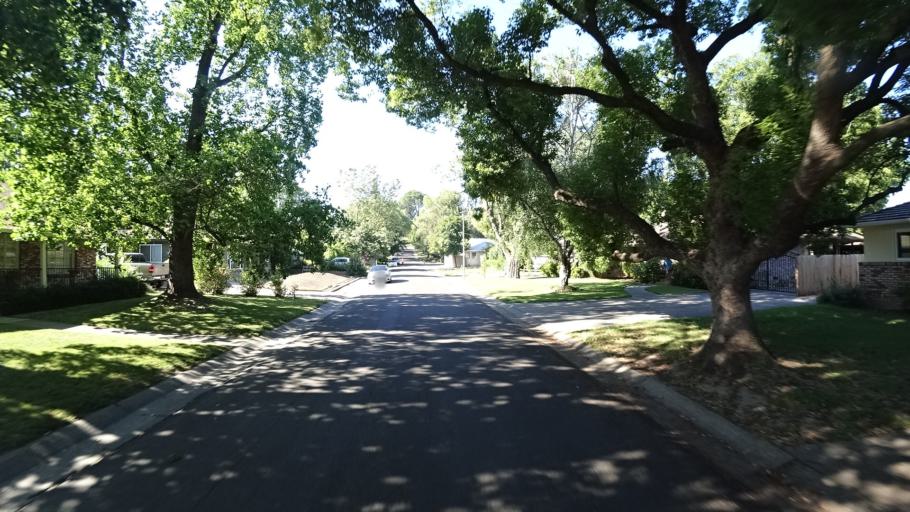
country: US
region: California
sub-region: Sacramento County
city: Sacramento
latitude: 38.5341
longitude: -121.5086
